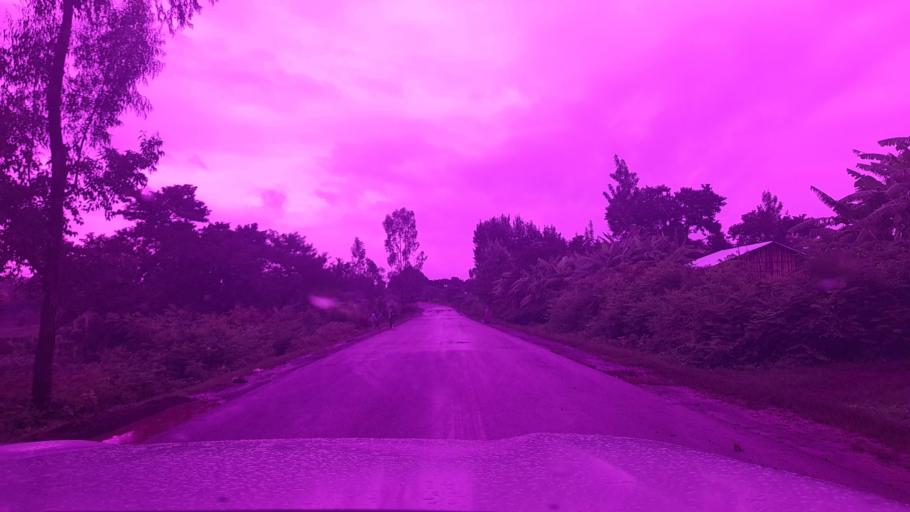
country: ET
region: Oromiya
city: Jima
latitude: 7.7149
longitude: 37.2533
